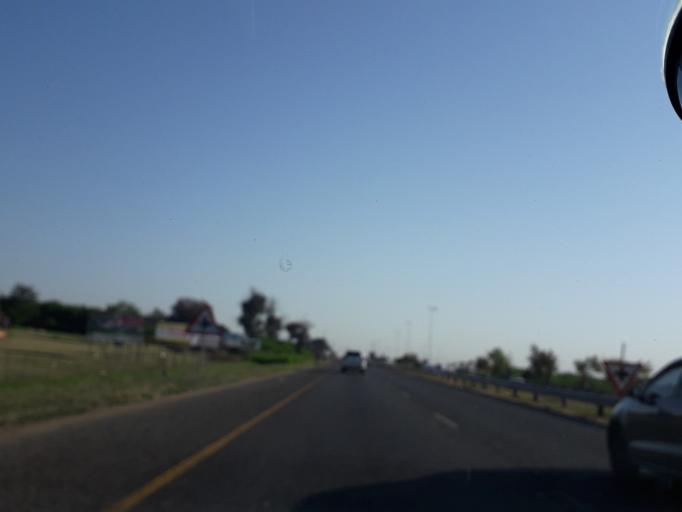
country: ZA
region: Gauteng
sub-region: City of Johannesburg Metropolitan Municipality
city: Roodepoort
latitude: -26.0848
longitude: 27.9301
